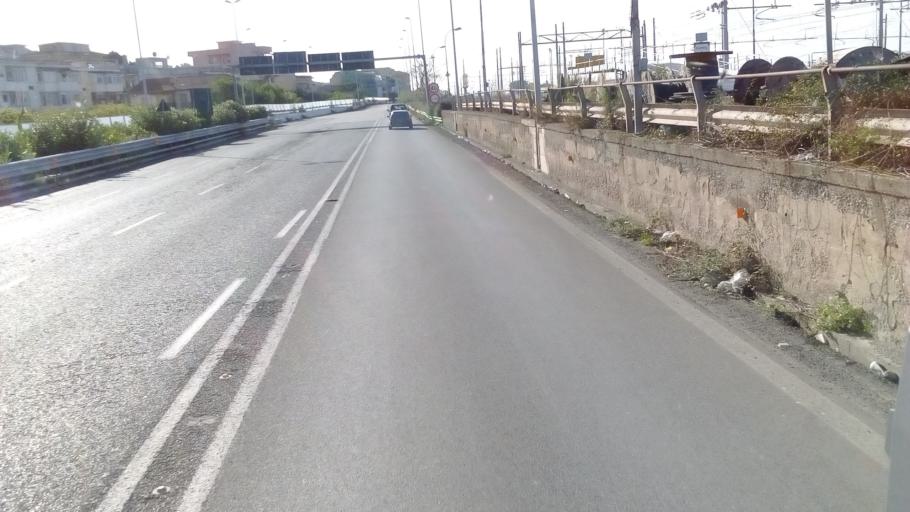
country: IT
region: Calabria
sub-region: Provincia di Reggio Calabria
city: Campo Calabro
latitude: 38.2125
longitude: 15.6353
